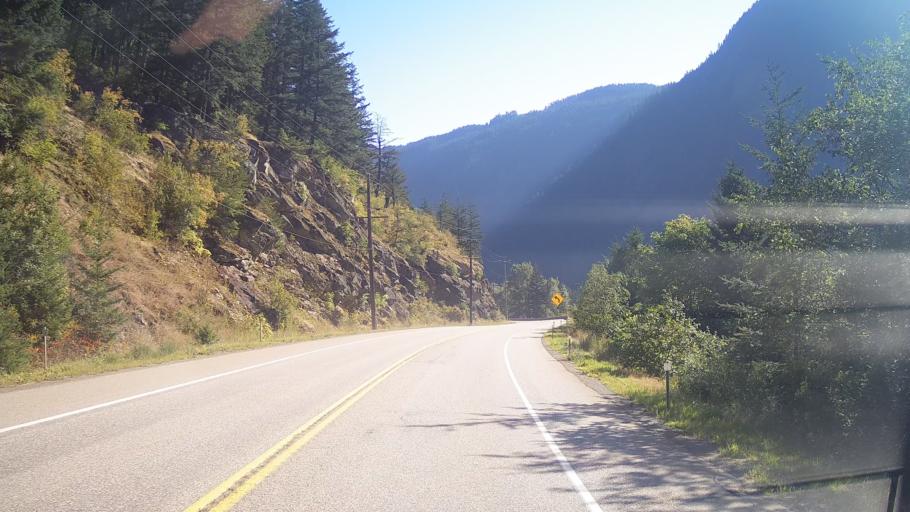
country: CA
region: British Columbia
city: Hope
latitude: 49.6158
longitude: -121.4094
